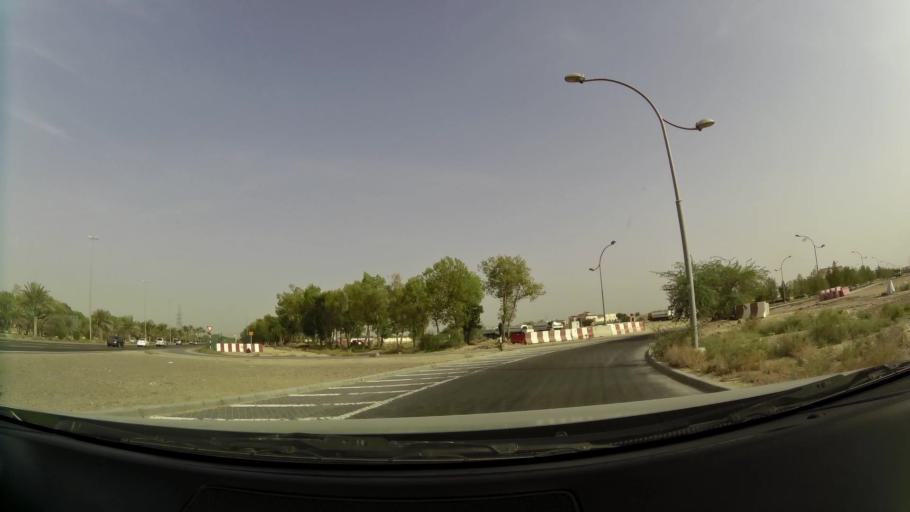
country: AE
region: Abu Dhabi
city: Al Ain
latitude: 24.1342
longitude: 55.7231
